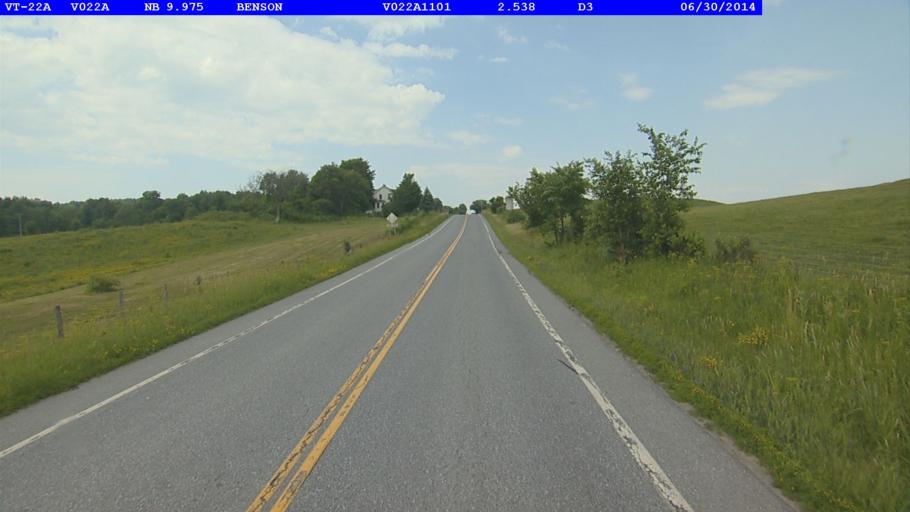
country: US
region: Vermont
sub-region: Rutland County
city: Fair Haven
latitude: 43.7050
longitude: -73.2962
